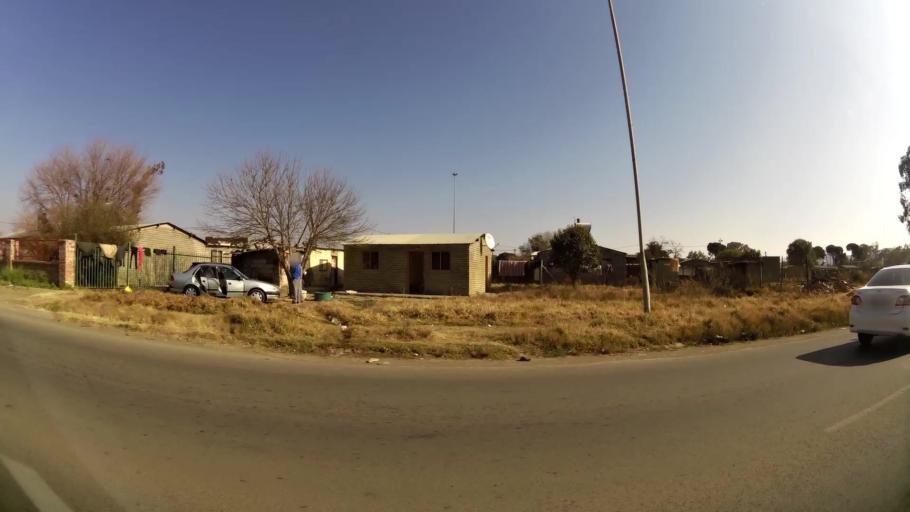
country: ZA
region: Orange Free State
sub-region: Mangaung Metropolitan Municipality
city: Bloemfontein
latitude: -29.1321
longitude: 26.2354
